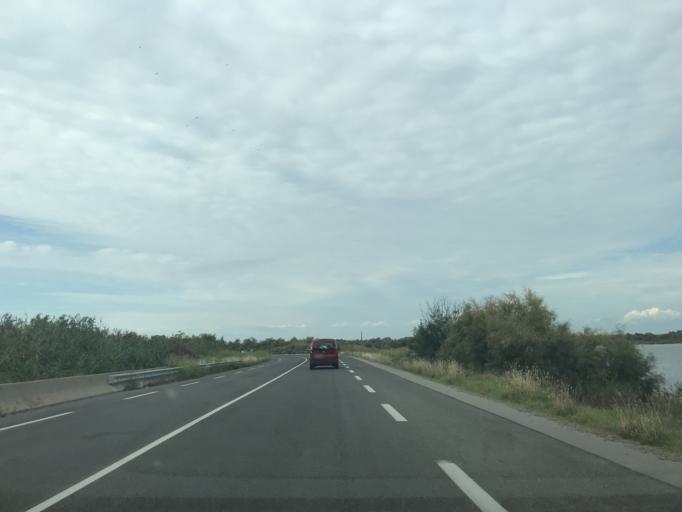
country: FR
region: Languedoc-Roussillon
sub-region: Departement du Gard
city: Le Grau-du-Roi
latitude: 43.5511
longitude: 4.1330
